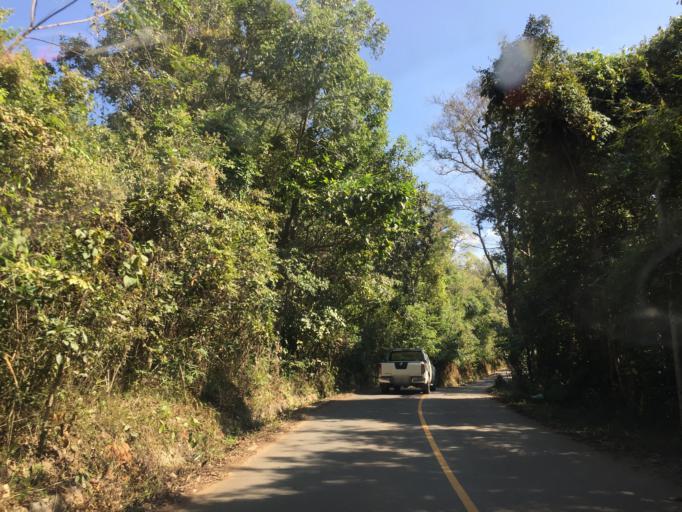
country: TH
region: Chiang Mai
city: Samoeng
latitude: 18.9491
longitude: 98.7932
